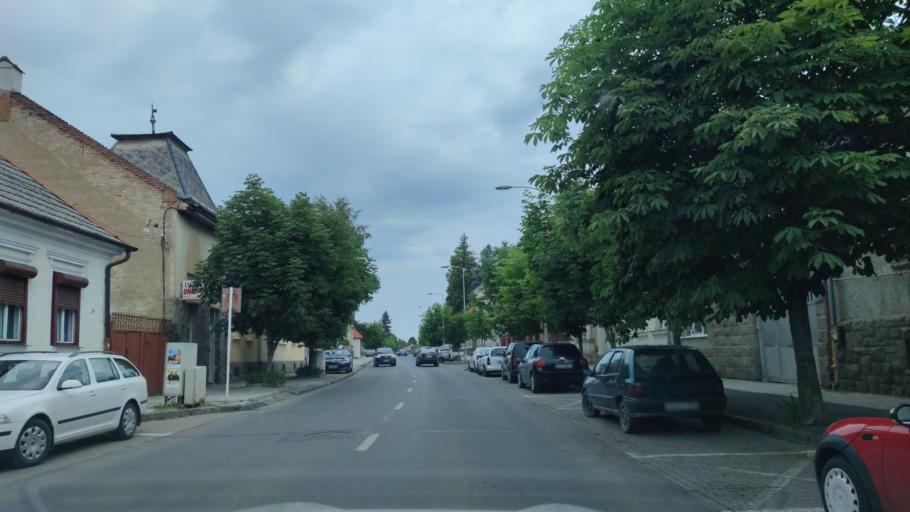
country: RO
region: Harghita
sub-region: Municipiul Miercurea Ciuc
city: Miercurea-Ciuc
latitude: 46.3655
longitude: 25.8062
